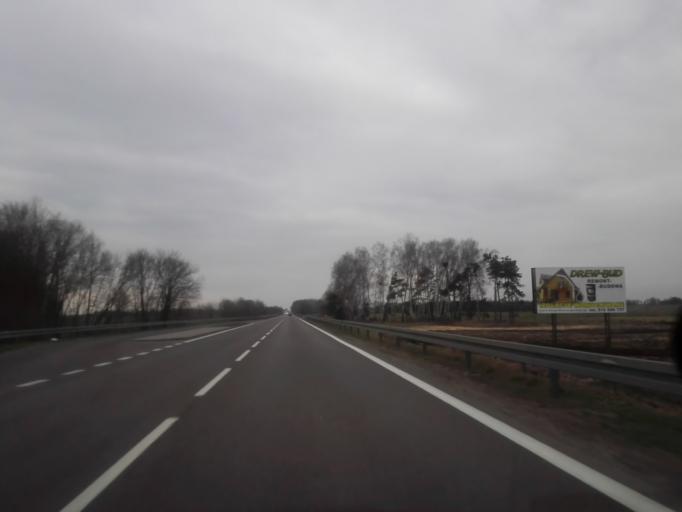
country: PL
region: Podlasie
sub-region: Powiat grajewski
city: Rajgrod
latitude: 53.6807
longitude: 22.6083
